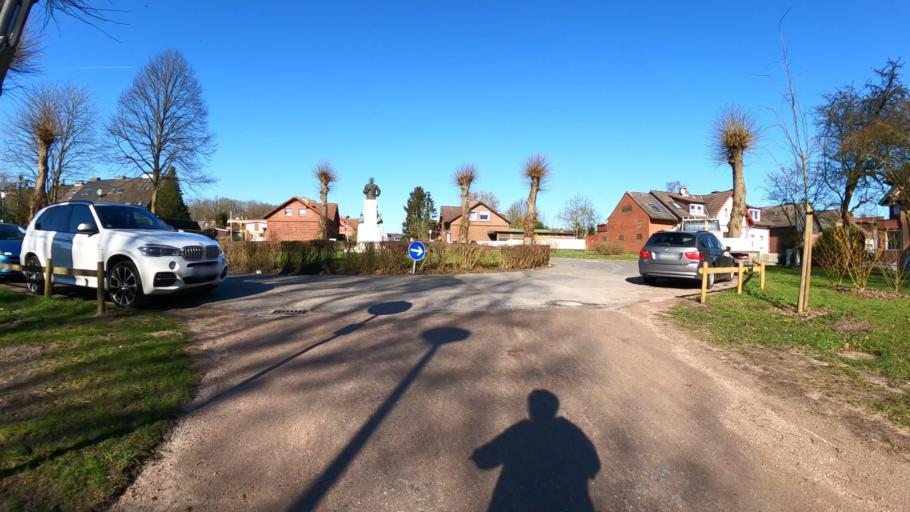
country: DE
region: Schleswig-Holstein
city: Pinneberg
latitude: 53.6634
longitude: 9.7884
